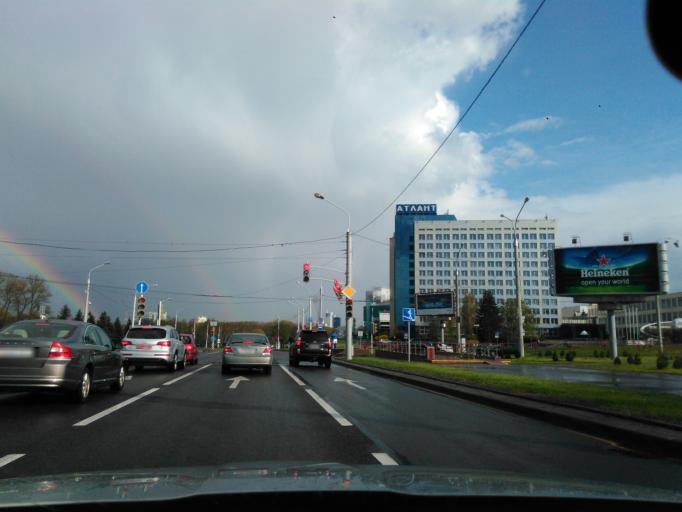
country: BY
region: Minsk
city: Minsk
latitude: 53.9251
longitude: 27.5226
